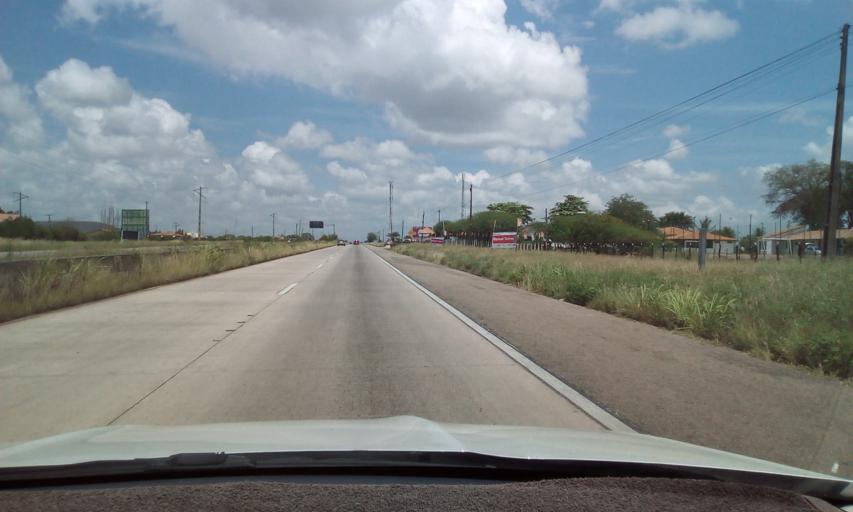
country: BR
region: Pernambuco
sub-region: Gravata
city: Gravata
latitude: -8.2161
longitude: -35.6453
